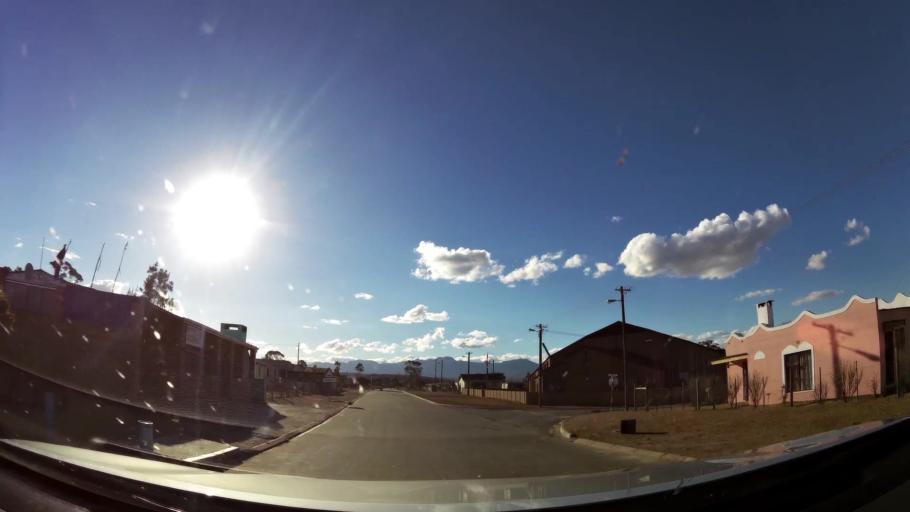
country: ZA
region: Western Cape
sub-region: Eden District Municipality
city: Riversdale
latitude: -34.1040
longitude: 20.9665
